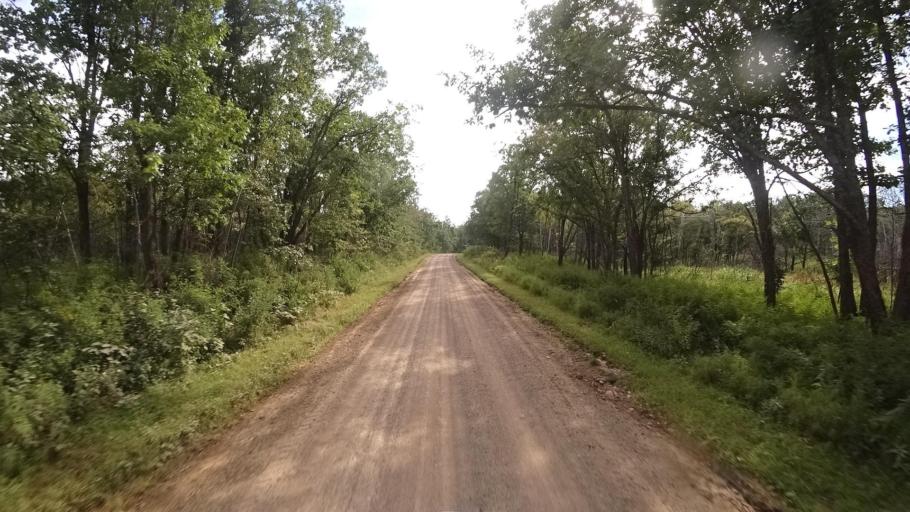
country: RU
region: Primorskiy
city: Dostoyevka
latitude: 44.3557
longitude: 133.5222
